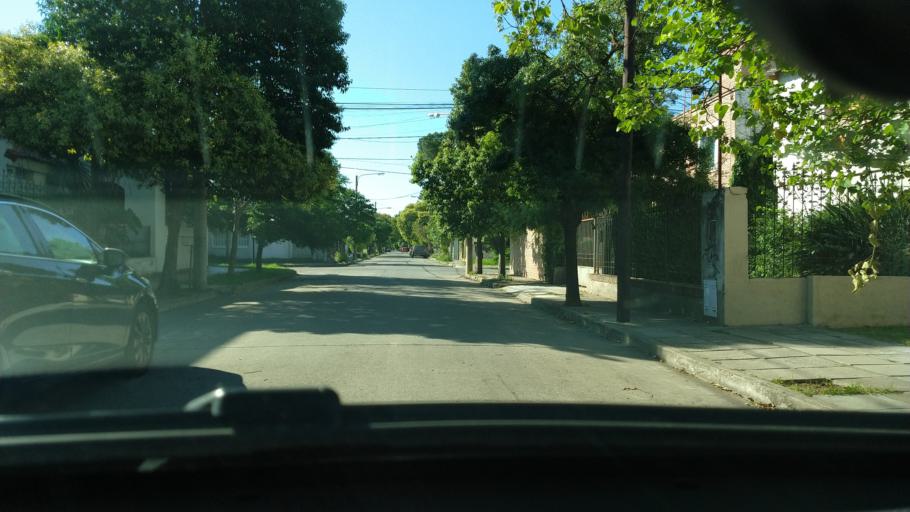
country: AR
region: Cordoba
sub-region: Departamento de Capital
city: Cordoba
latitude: -31.3659
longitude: -64.2296
